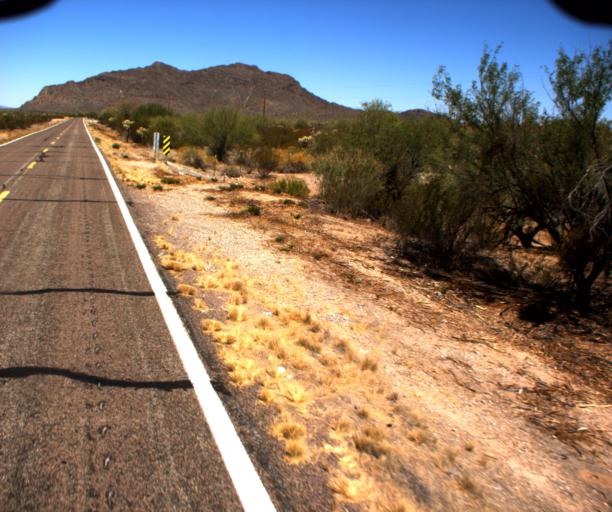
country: US
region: Arizona
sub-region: Pima County
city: Ajo
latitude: 32.2208
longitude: -112.6635
